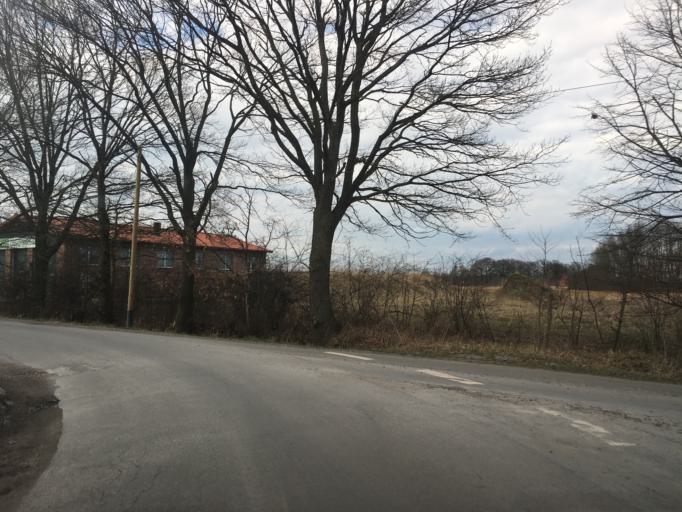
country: DE
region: North Rhine-Westphalia
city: Ludinghausen
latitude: 51.7860
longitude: 7.4651
